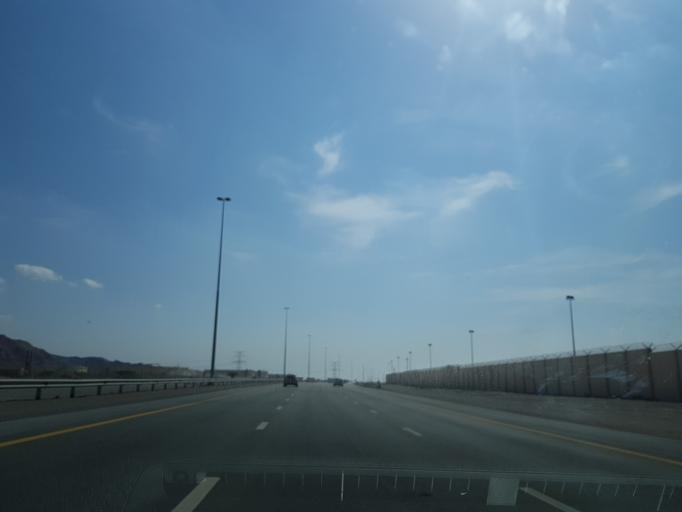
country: AE
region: Ra's al Khaymah
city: Ras al-Khaimah
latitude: 25.7786
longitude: 56.0301
